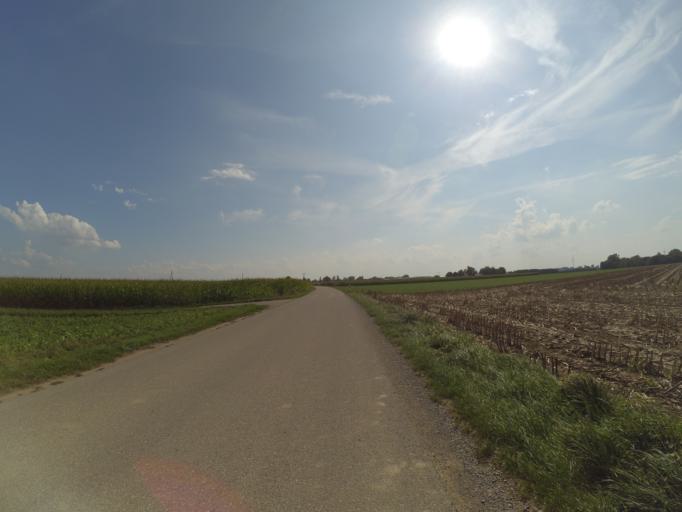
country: DE
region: Bavaria
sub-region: Swabia
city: Lamerdingen
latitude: 48.0951
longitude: 10.7697
